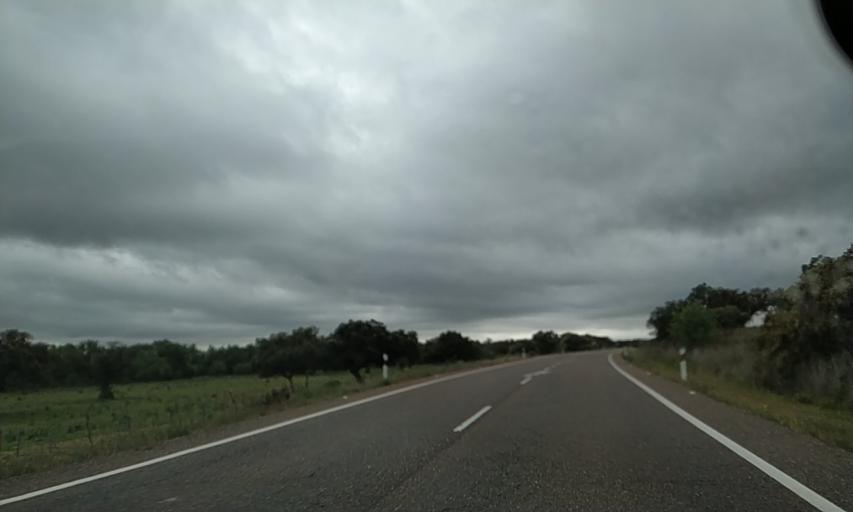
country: ES
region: Extremadura
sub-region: Provincia de Badajoz
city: La Roca de la Sierra
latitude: 39.0714
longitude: -6.7550
